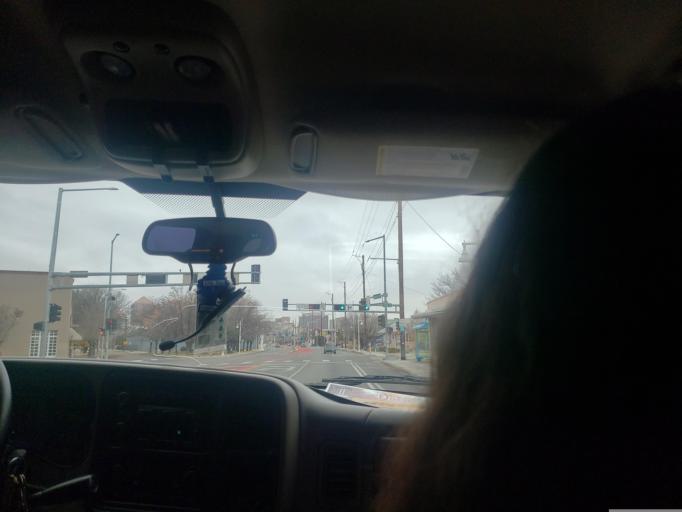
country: US
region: New Mexico
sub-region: Bernalillo County
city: Albuquerque
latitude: 35.0874
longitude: -106.6647
